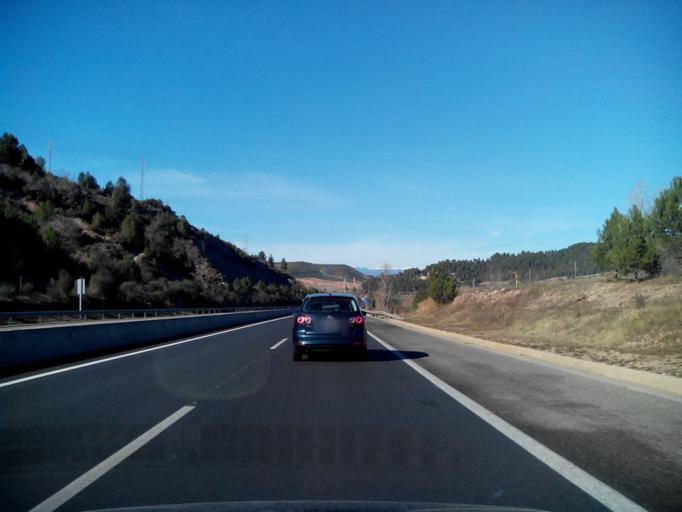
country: ES
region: Catalonia
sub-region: Provincia de Barcelona
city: Sallent
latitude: 41.8242
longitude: 1.8890
